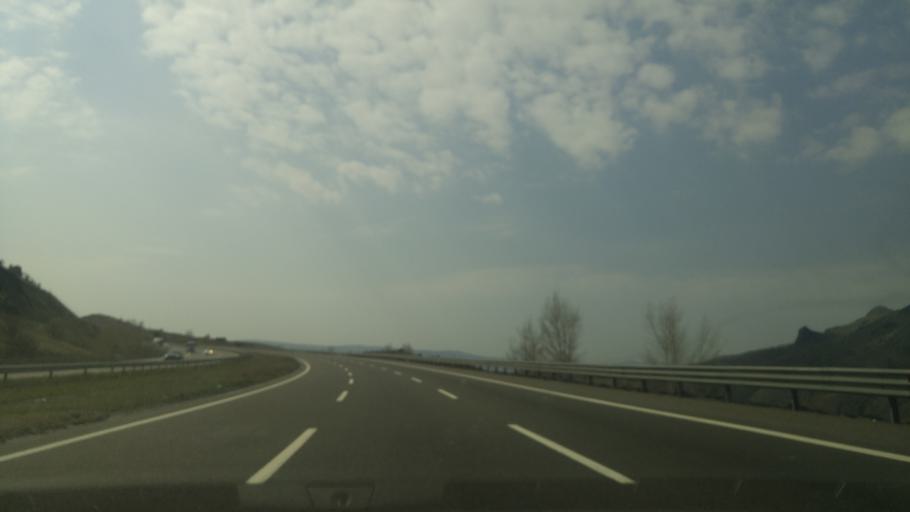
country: TR
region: Ankara
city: Celtikci
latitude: 40.3667
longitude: 32.4640
